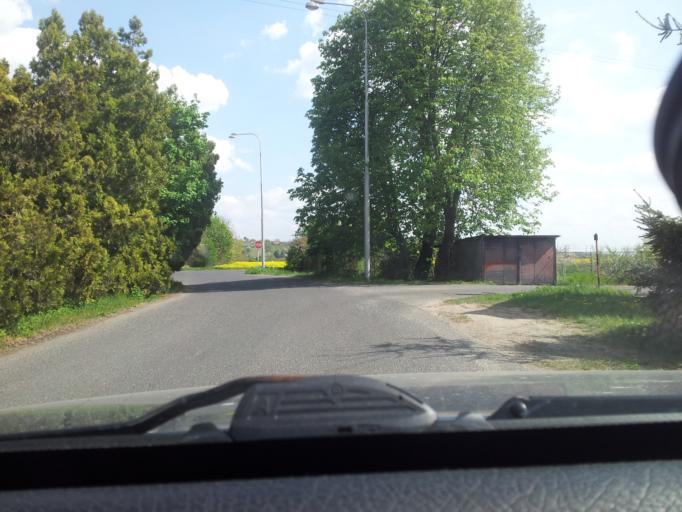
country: SK
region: Nitriansky
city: Levice
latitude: 48.2071
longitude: 18.6179
